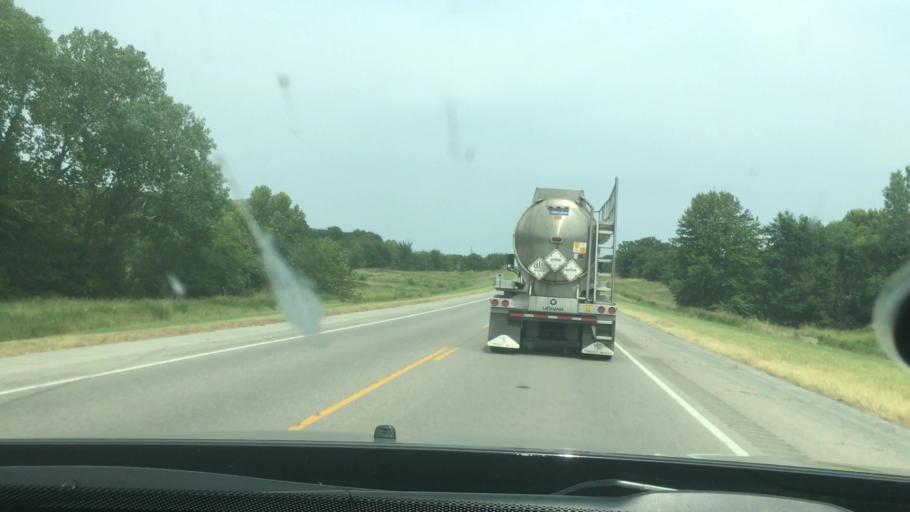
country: US
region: Oklahoma
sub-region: Pontotoc County
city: Ada
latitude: 34.6302
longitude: -96.4687
